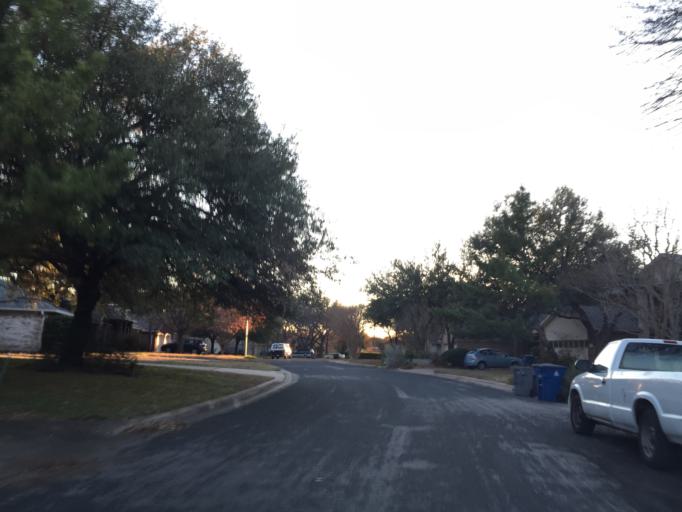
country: US
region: Texas
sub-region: Williamson County
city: Jollyville
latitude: 30.4401
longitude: -97.7619
